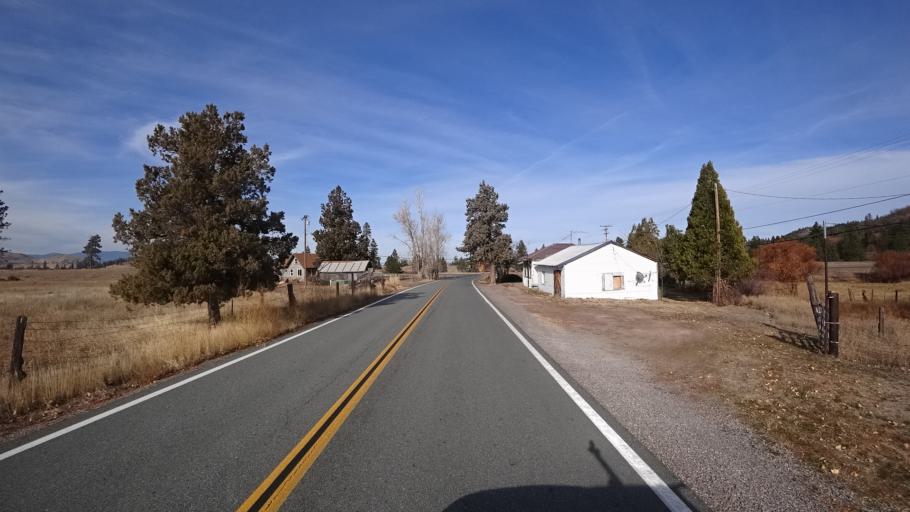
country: US
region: California
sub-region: Siskiyou County
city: Weed
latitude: 41.4393
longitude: -122.4354
